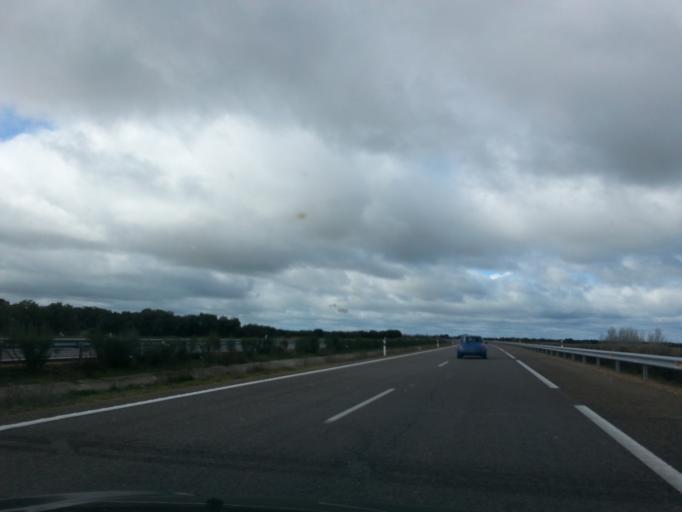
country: ES
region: Castille and Leon
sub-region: Provincia de Salamanca
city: San Munoz
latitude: 40.8064
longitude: -6.1890
